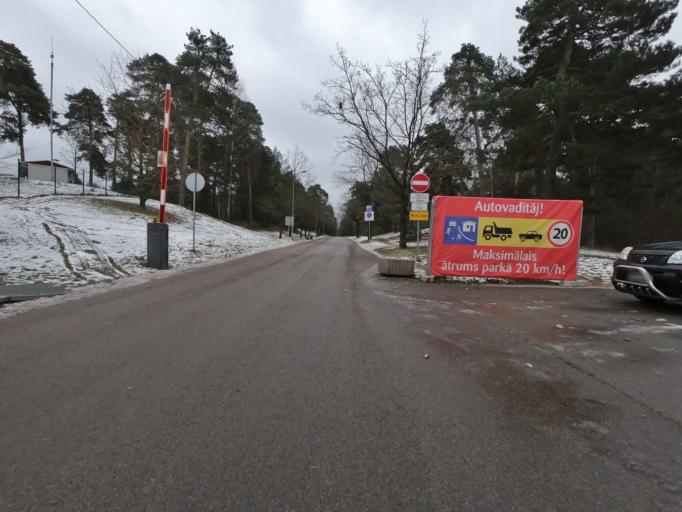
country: LV
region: Riga
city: Jaunciems
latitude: 57.0198
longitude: 24.1377
